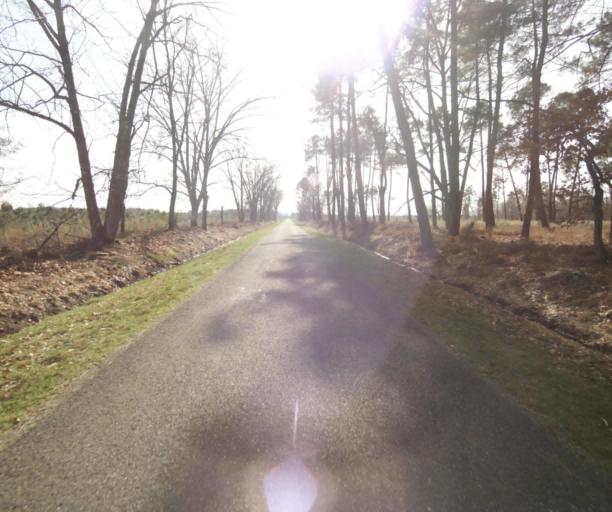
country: FR
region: Aquitaine
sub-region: Departement des Landes
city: Roquefort
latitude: 44.1567
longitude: -0.1693
